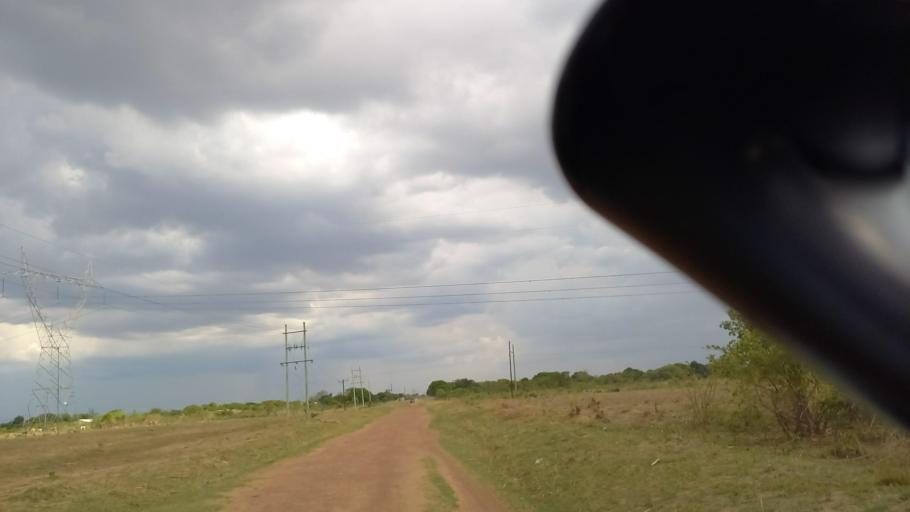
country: ZM
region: Lusaka
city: Kafue
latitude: -15.8475
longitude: 28.1031
